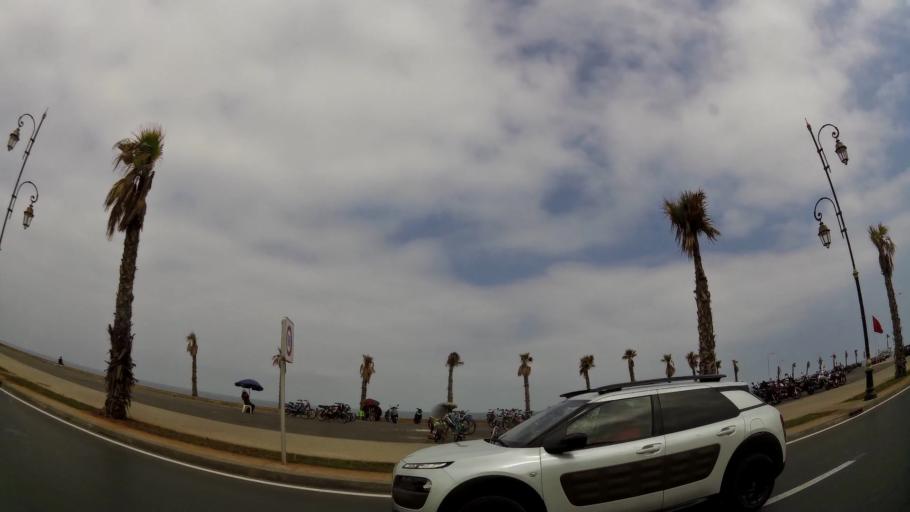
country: MA
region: Rabat-Sale-Zemmour-Zaer
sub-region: Rabat
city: Rabat
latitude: 34.0284
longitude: -6.8459
